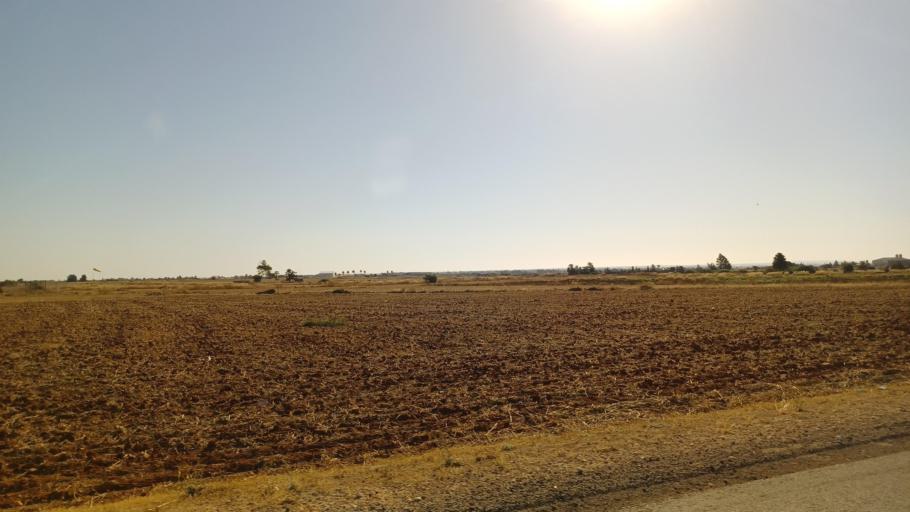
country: CY
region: Larnaka
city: Pyla
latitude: 35.0103
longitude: 33.7129
